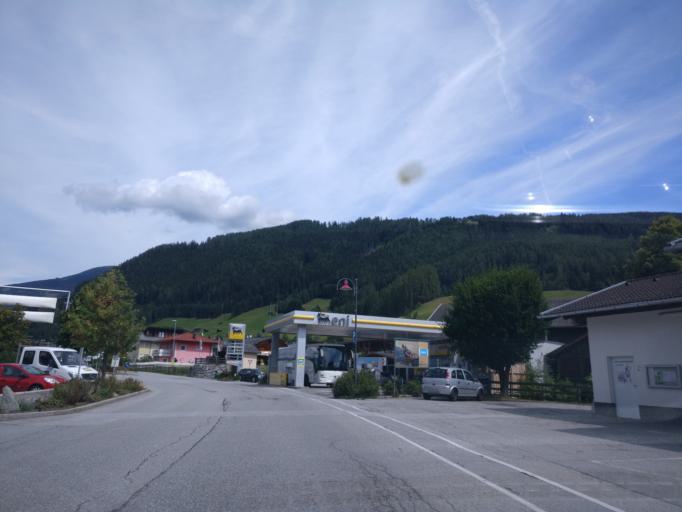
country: AT
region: Tyrol
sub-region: Politischer Bezirk Innsbruck Land
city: Mieders
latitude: 47.1709
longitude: 11.3831
